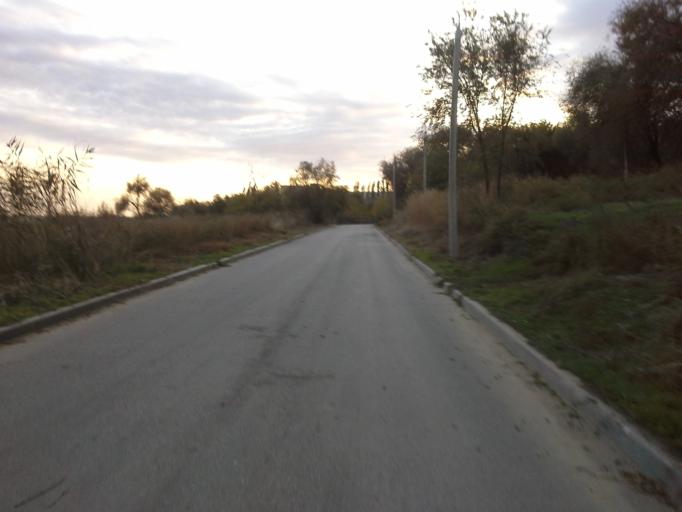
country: RU
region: Volgograd
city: Vodstroy
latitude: 48.8216
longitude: 44.6434
